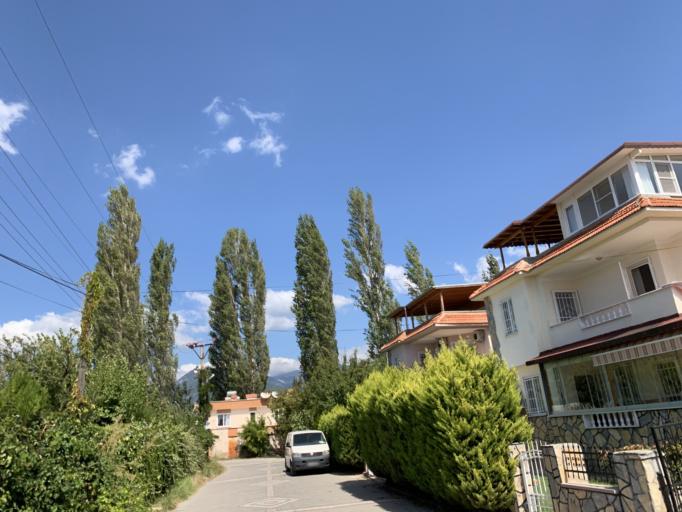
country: TR
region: Balikesir
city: Altinoluk
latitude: 39.5625
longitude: 26.8347
